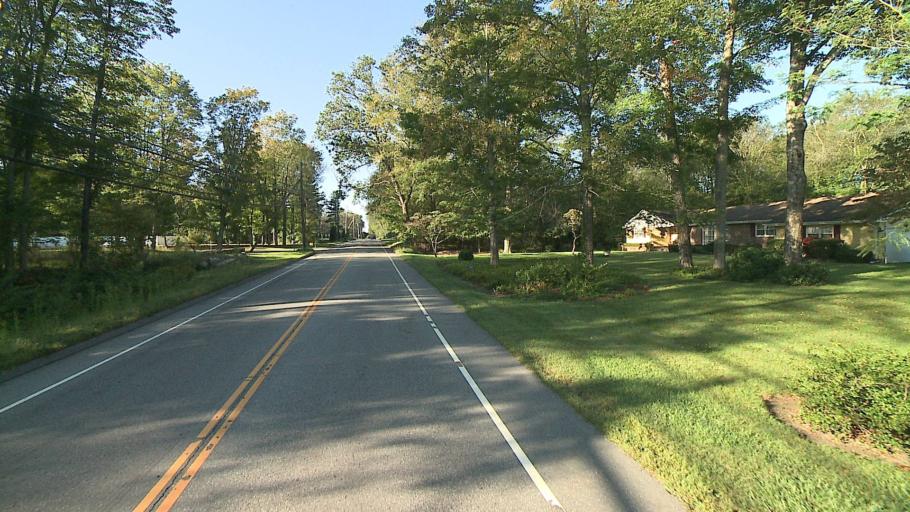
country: US
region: Connecticut
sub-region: Windham County
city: East Brooklyn
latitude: 41.7765
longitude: -71.8950
